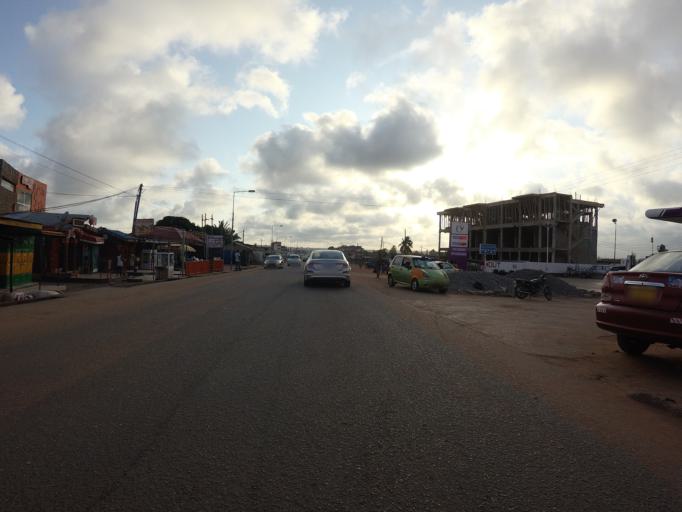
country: GH
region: Greater Accra
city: Teshi Old Town
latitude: 5.6071
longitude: -0.1134
